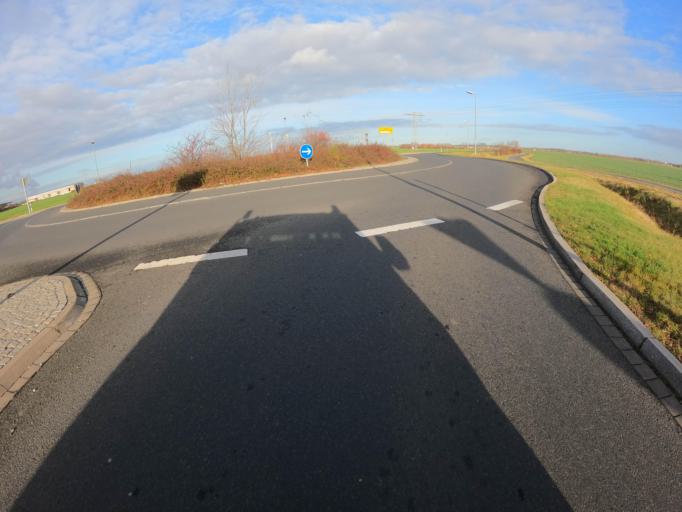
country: DE
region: Saxony
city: Markranstadt
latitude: 51.3154
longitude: 12.2318
